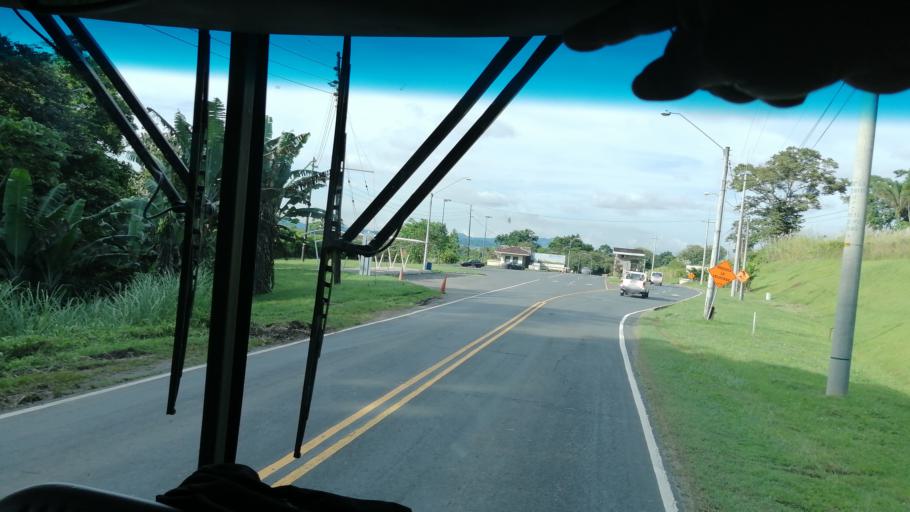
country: PA
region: Panama
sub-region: Distrito de Panama
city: Ancon
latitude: 8.9487
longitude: -79.5902
